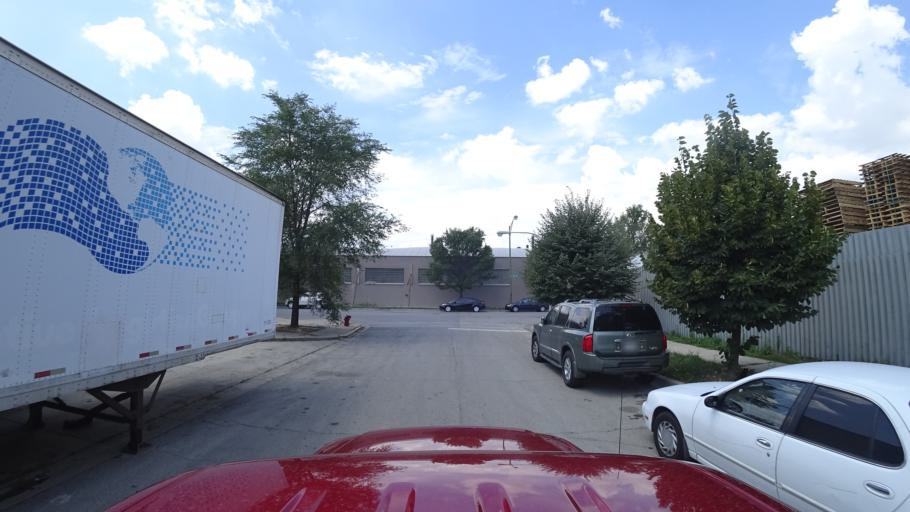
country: US
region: Illinois
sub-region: Cook County
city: Chicago
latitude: 41.8199
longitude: -87.6405
